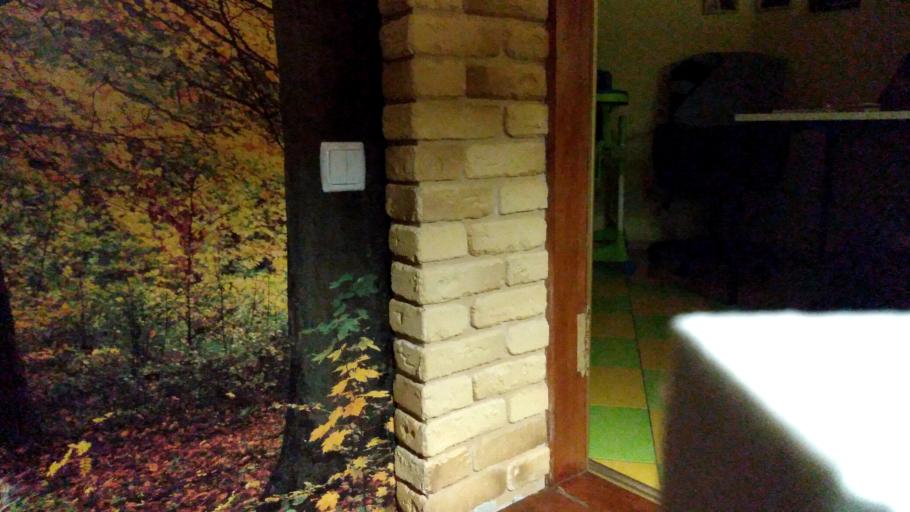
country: RU
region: Vologda
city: Lipin Bor
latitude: 60.7866
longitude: 38.0380
